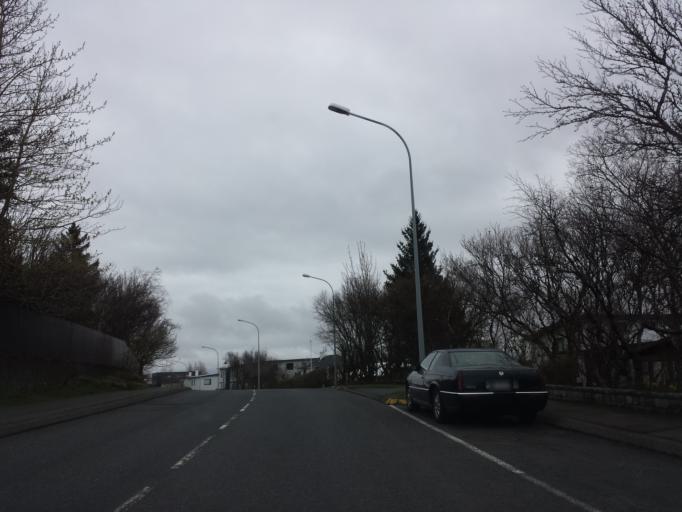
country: IS
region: Capital Region
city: Kopavogur
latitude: 64.1094
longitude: -21.9330
